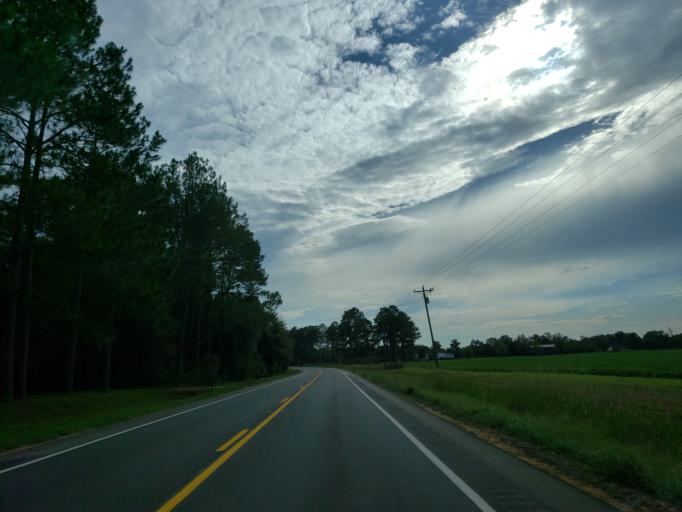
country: US
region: Georgia
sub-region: Irwin County
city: Ocilla
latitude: 31.5754
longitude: -83.3002
